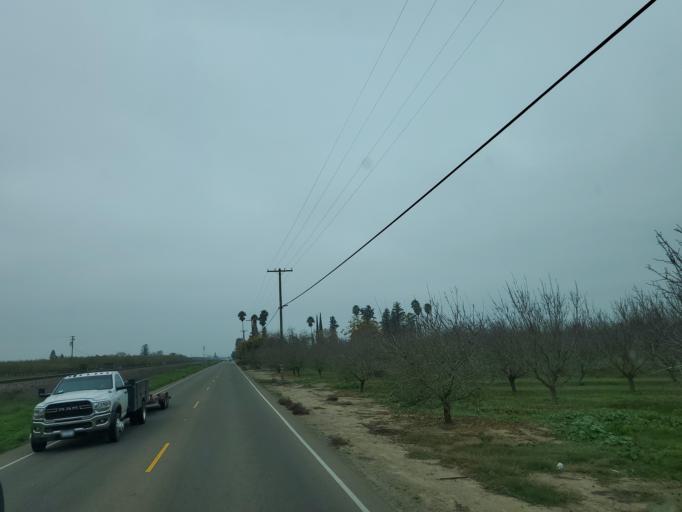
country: US
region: California
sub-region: Stanislaus County
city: Hughson
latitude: 37.5826
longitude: -120.8545
